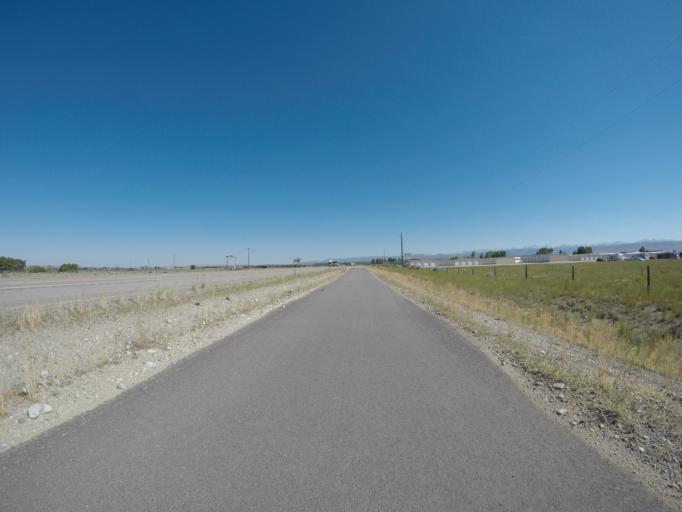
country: US
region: Wyoming
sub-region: Sublette County
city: Pinedale
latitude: 42.8355
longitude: -109.8464
